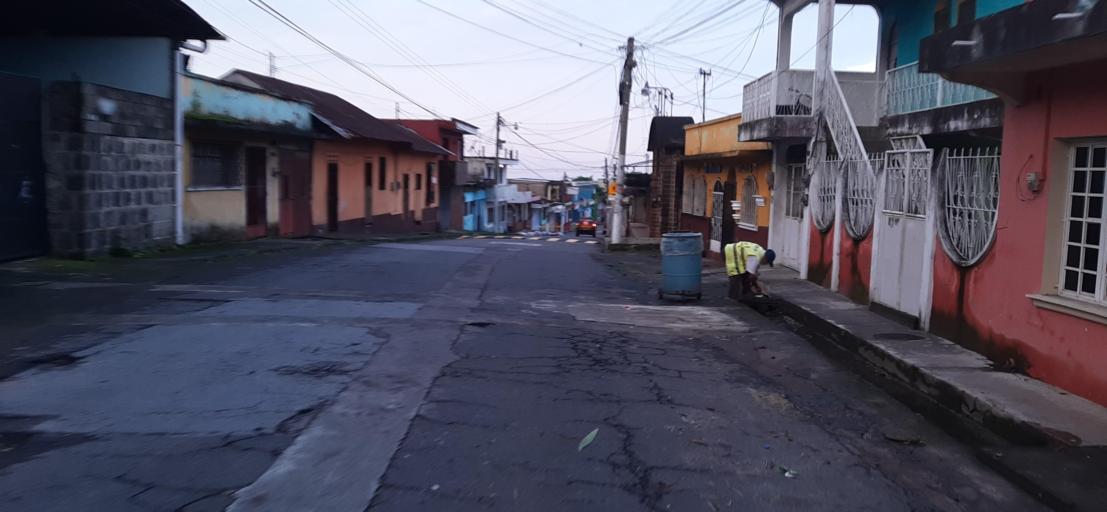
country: GT
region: Retalhuleu
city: San Felipe
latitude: 14.6264
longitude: -91.5917
